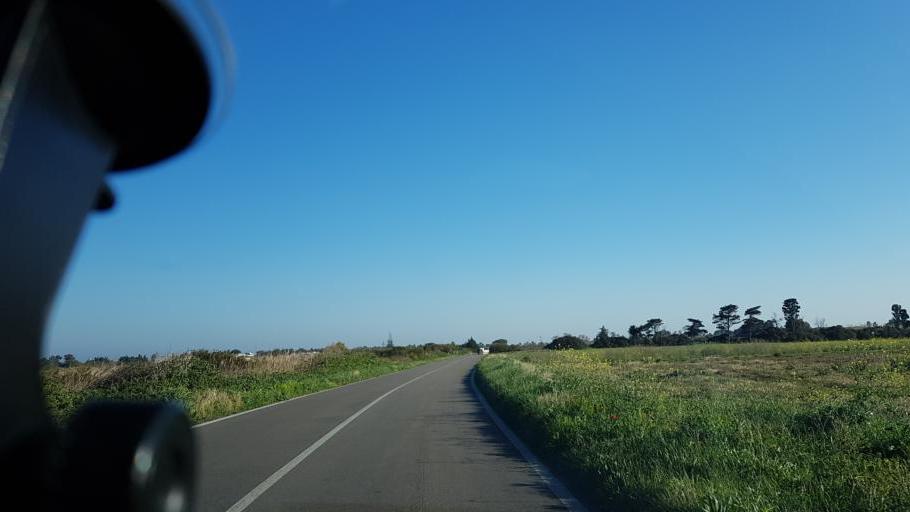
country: IT
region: Apulia
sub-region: Provincia di Lecce
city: Giorgilorio
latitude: 40.4368
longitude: 18.2388
